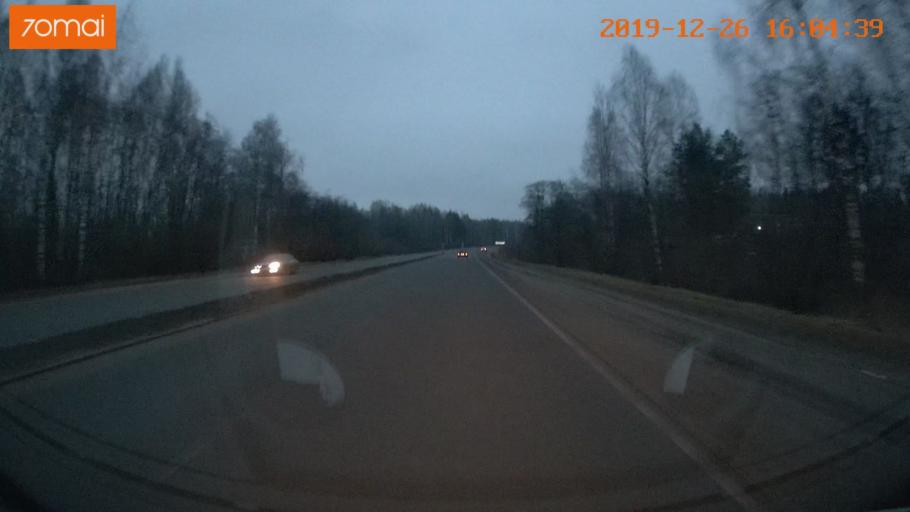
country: RU
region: Jaroslavl
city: Rybinsk
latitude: 58.0085
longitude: 38.8756
